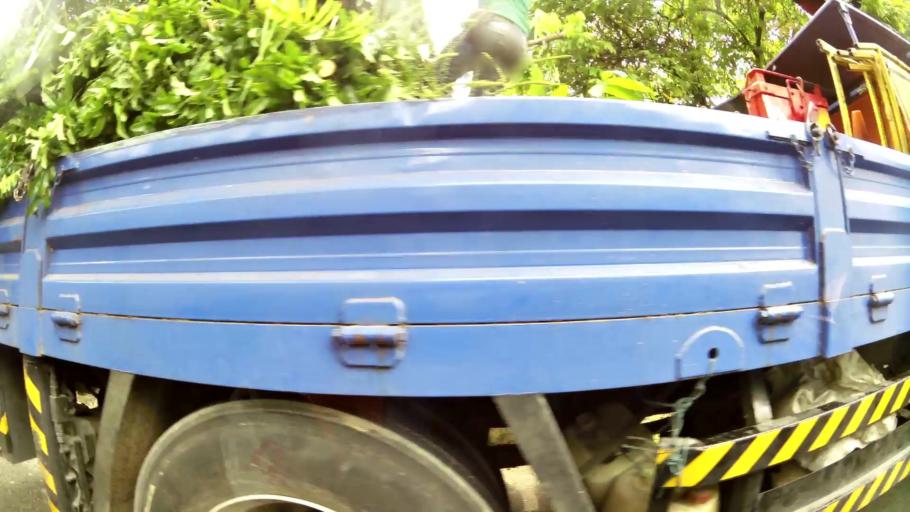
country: SG
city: Singapore
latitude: 1.3354
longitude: 103.8031
